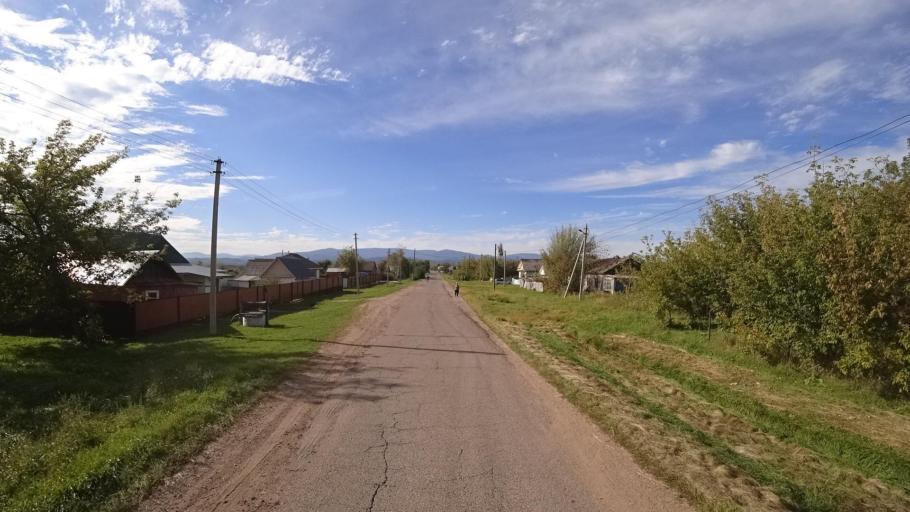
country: RU
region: Primorskiy
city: Dostoyevka
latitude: 44.2989
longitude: 133.4516
